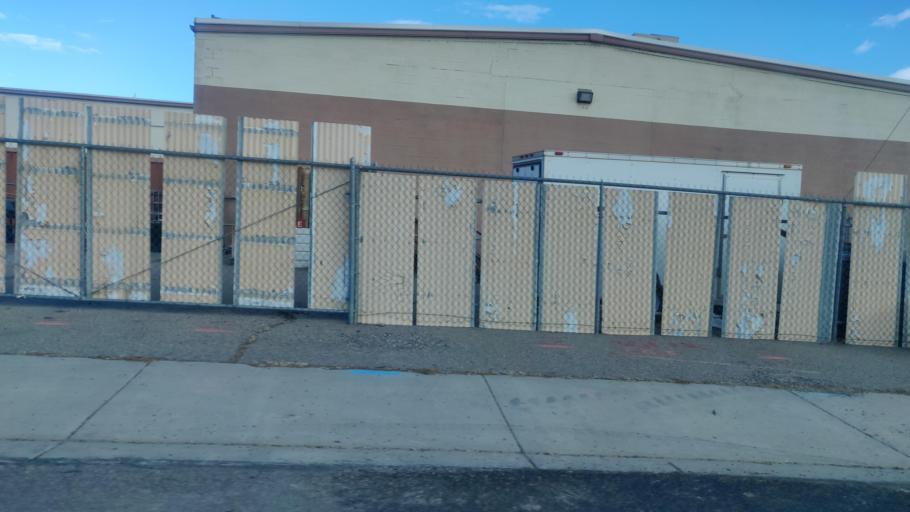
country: US
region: Colorado
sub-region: Mesa County
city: Grand Junction
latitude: 39.0698
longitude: -108.5731
